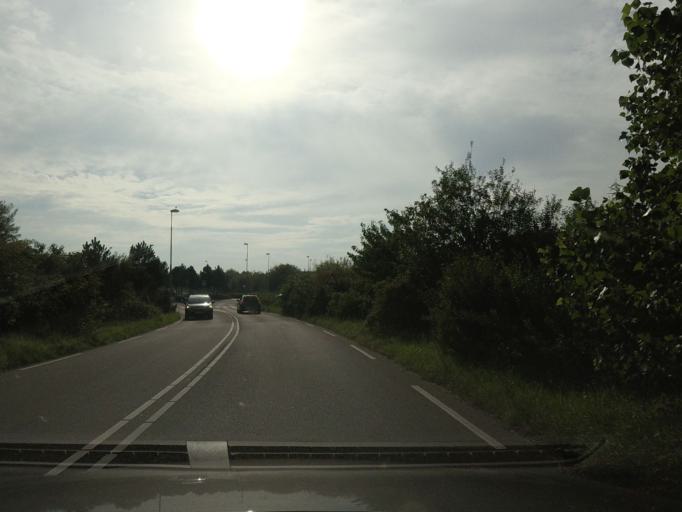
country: NL
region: North Holland
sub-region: Gemeente Den Helder
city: Den Helder
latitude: 52.8848
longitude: 4.7352
